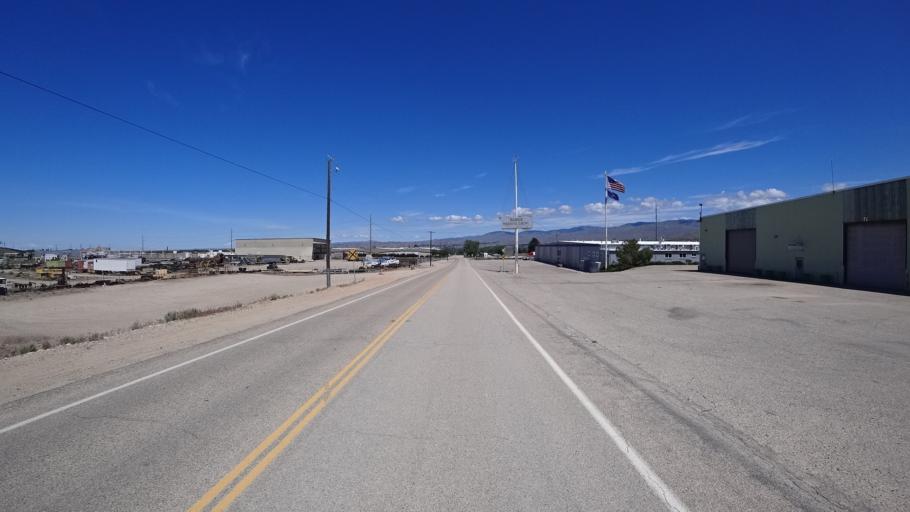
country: US
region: Idaho
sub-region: Ada County
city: Boise
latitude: 43.5612
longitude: -116.1834
